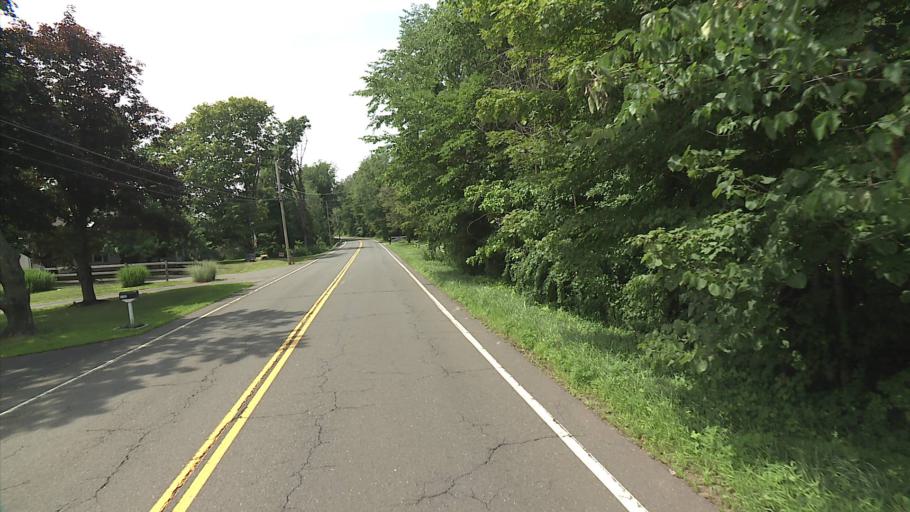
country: US
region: Connecticut
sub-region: Middlesex County
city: Durham
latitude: 41.4257
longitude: -72.7366
